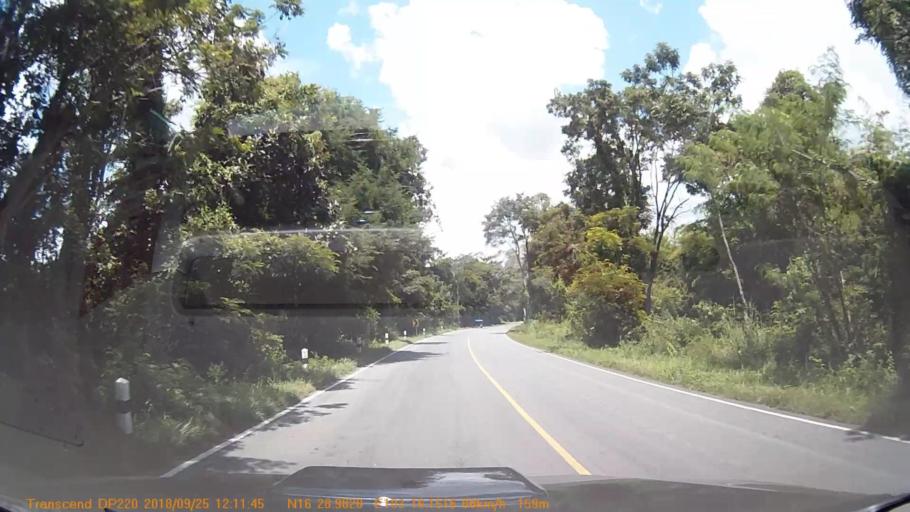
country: TH
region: Kalasin
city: Huai Mek
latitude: 16.4834
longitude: 103.2692
